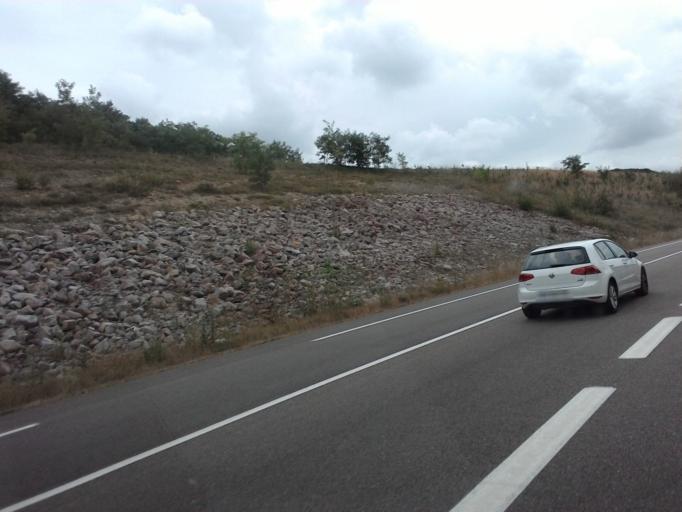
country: FR
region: Franche-Comte
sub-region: Departement du Jura
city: Montmorot
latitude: 46.6724
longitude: 5.5108
